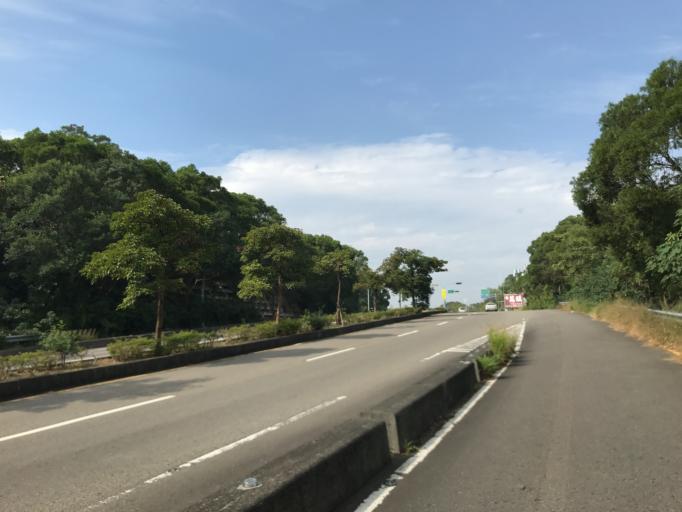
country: TW
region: Taiwan
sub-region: Hsinchu
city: Hsinchu
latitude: 24.7815
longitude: 120.9552
